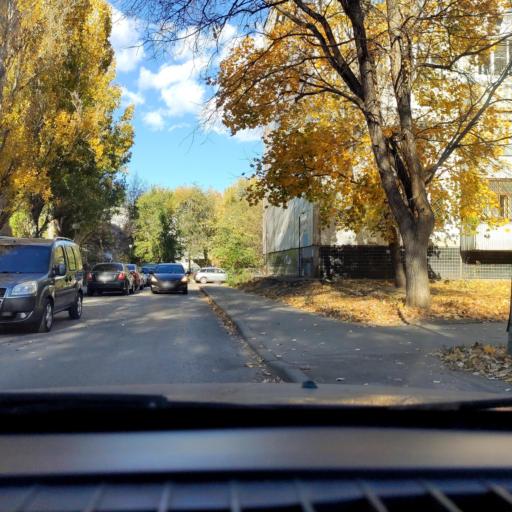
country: RU
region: Samara
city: Tol'yatti
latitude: 53.5115
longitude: 49.2876
